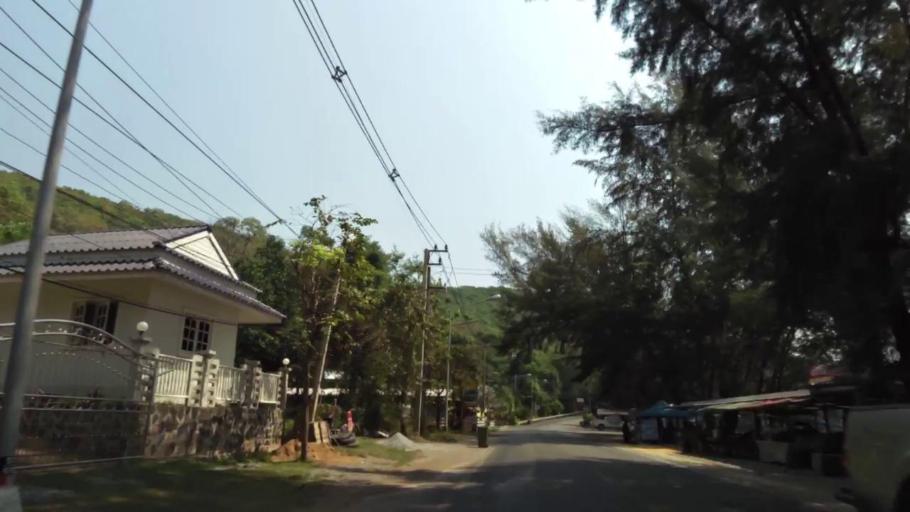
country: TH
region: Chanthaburi
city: Tha Mai
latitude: 12.5325
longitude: 101.9440
